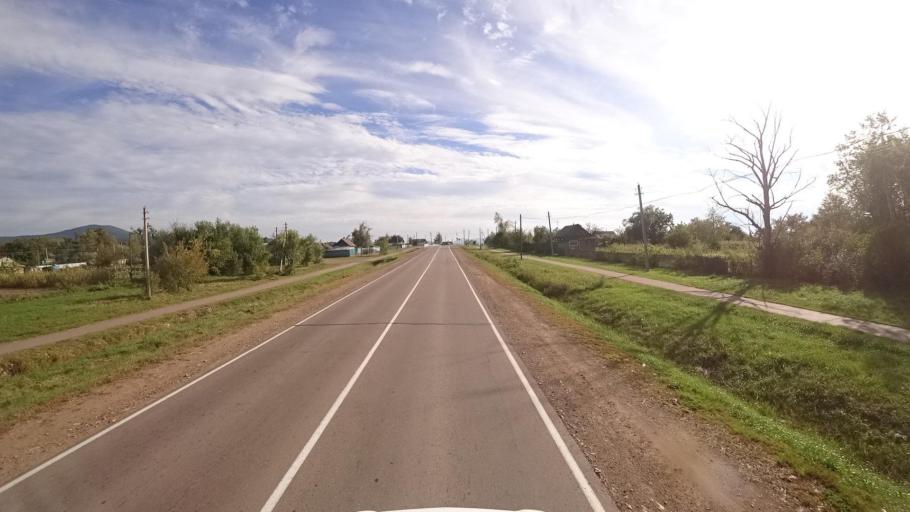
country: RU
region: Primorskiy
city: Dostoyevka
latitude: 44.3033
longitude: 133.4496
